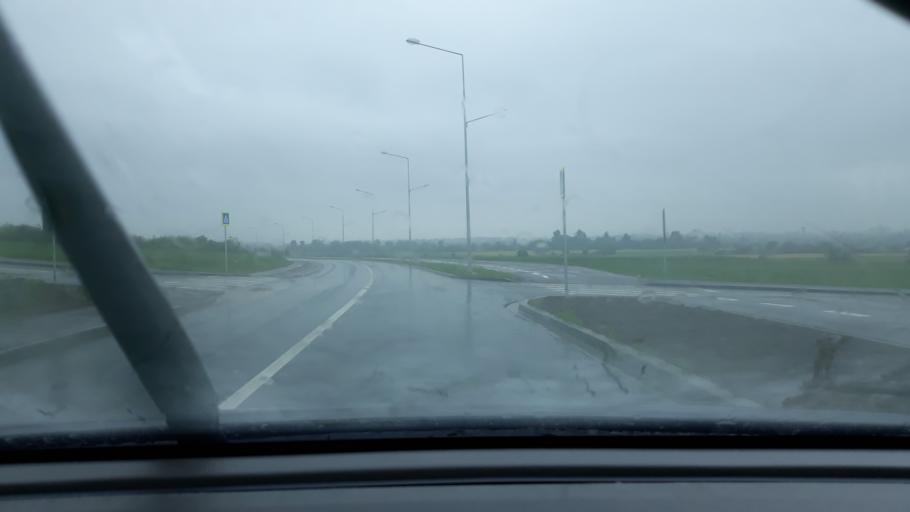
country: RO
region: Bihor
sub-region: Comuna Biharea
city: Biharea
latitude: 47.1052
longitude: 21.9075
